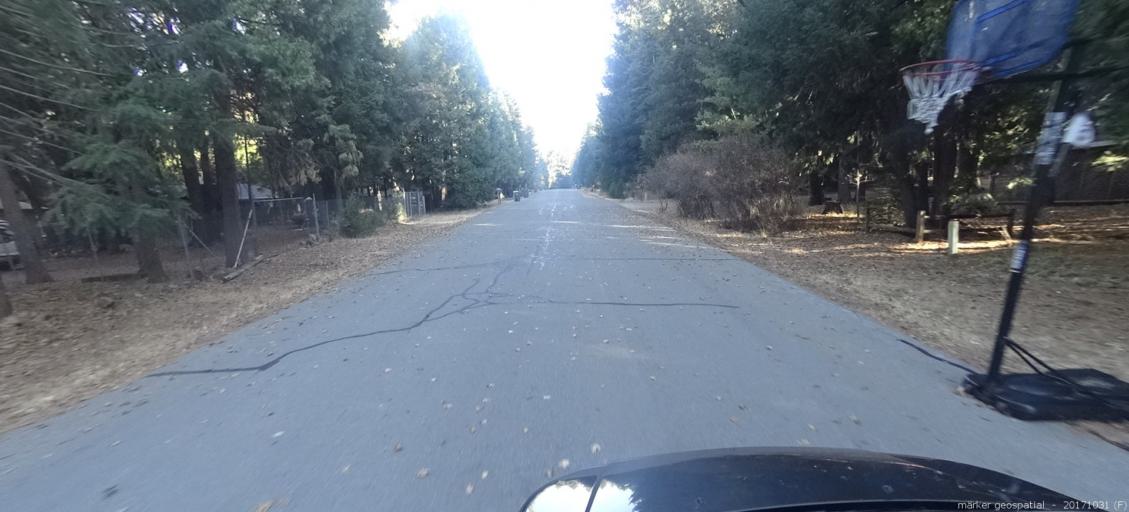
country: US
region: California
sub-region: Shasta County
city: Shingletown
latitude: 40.5221
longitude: -121.8002
